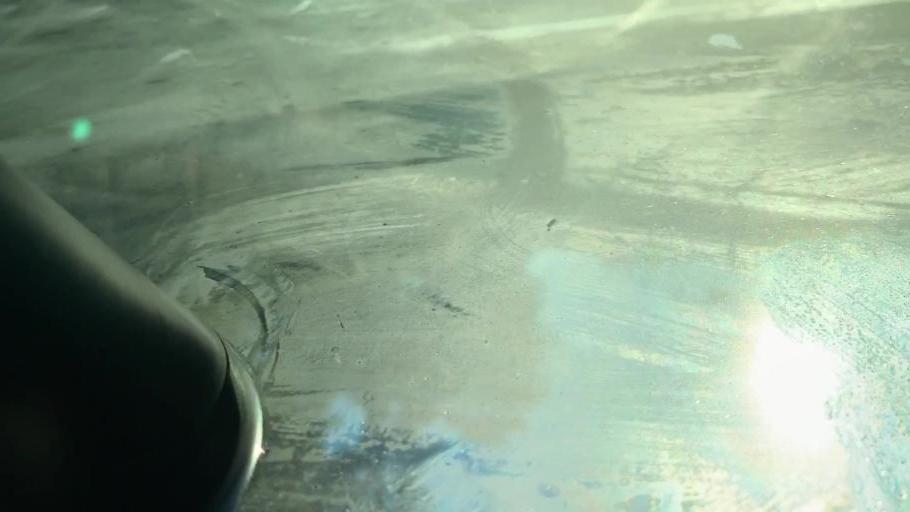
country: US
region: South Carolina
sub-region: Richland County
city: Dentsville
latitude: 34.0548
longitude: -80.9479
